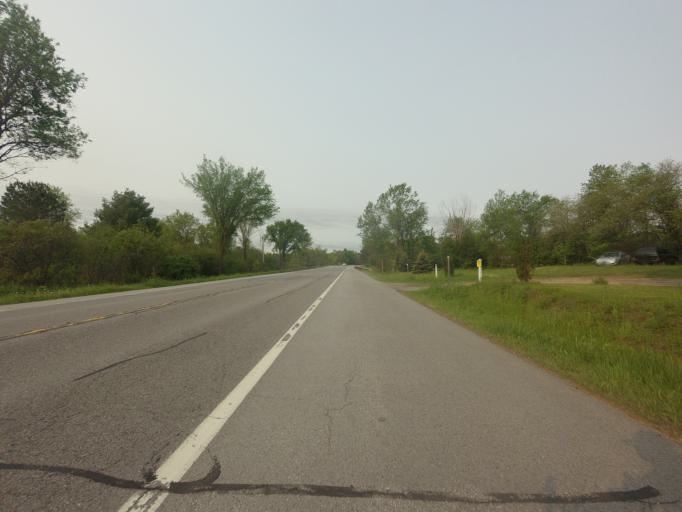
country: US
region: New York
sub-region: Jefferson County
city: Carthage
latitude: 44.0516
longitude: -75.5546
